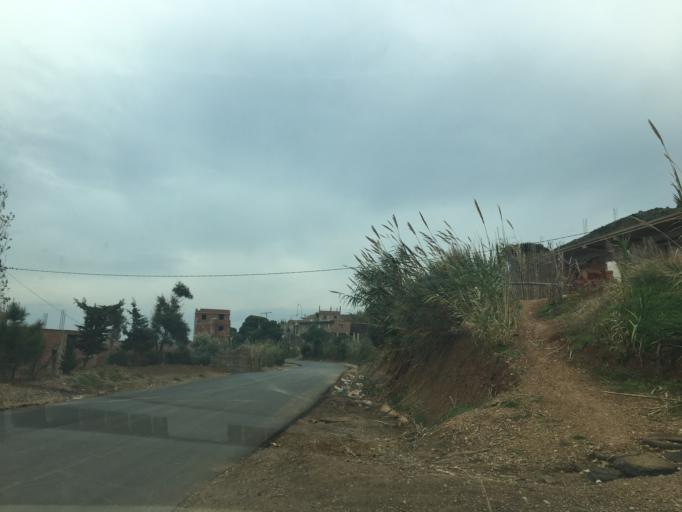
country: DZ
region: Tipaza
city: Tipasa
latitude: 36.6381
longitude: 2.3235
